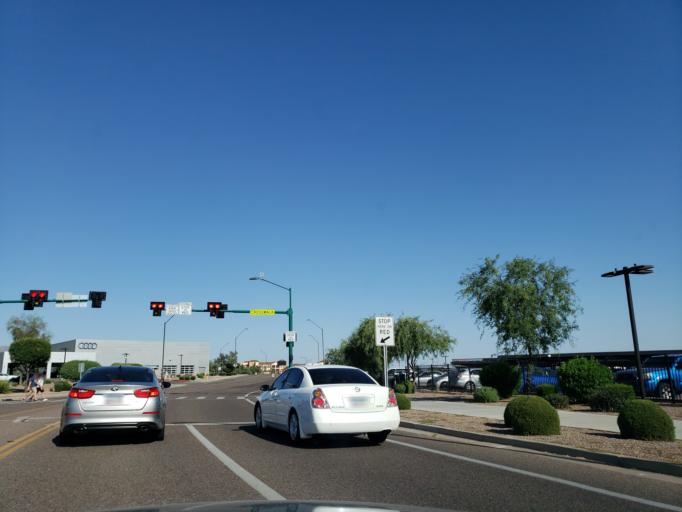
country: US
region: Arizona
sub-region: Maricopa County
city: Paradise Valley
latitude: 33.6477
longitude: -111.9283
